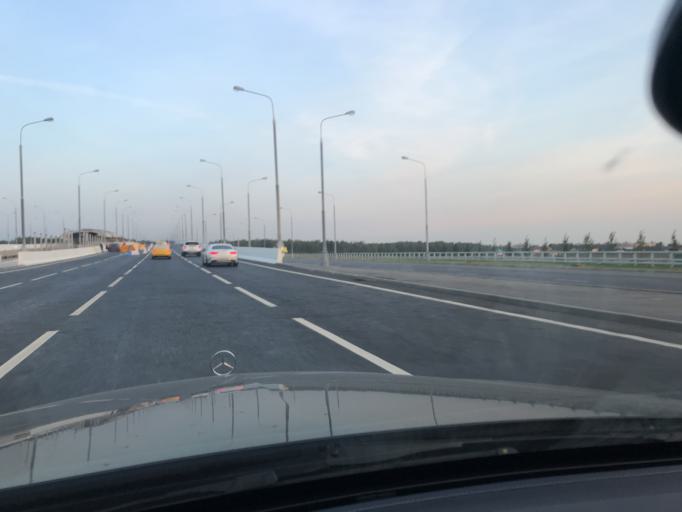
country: RU
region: Moskovskaya
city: Mosrentgen
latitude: 55.5857
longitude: 37.4346
